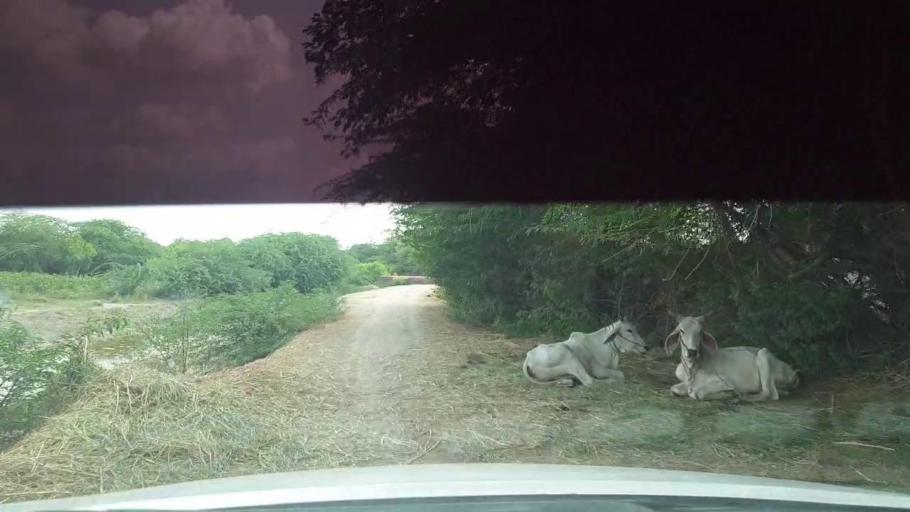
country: PK
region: Sindh
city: Kadhan
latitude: 24.6170
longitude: 69.0278
